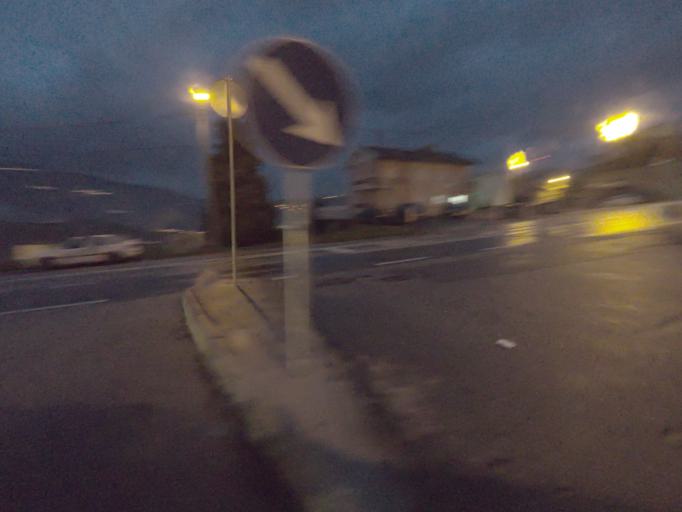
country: PT
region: Vila Real
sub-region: Peso da Regua
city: Peso da Regua
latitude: 41.1620
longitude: -7.7802
